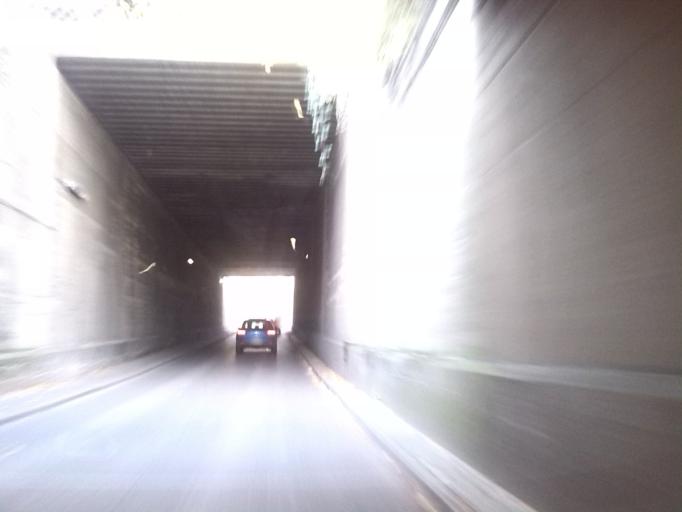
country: DE
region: Baden-Wuerttemberg
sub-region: Regierungsbezirk Stuttgart
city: Kornwestheim
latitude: 48.8788
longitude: 9.1846
